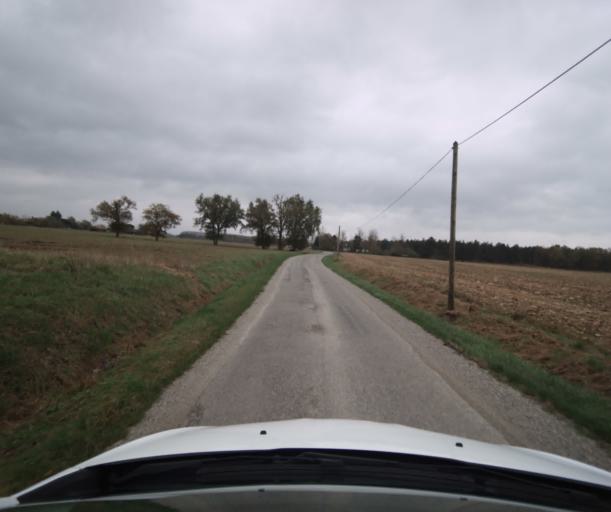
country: FR
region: Midi-Pyrenees
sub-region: Departement du Tarn-et-Garonne
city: Castelsarrasin
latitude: 44.0689
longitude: 1.1501
